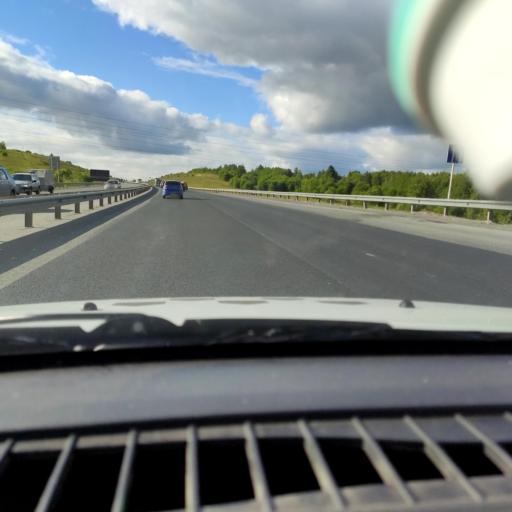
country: RU
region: Perm
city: Polazna
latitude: 58.1868
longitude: 56.4129
